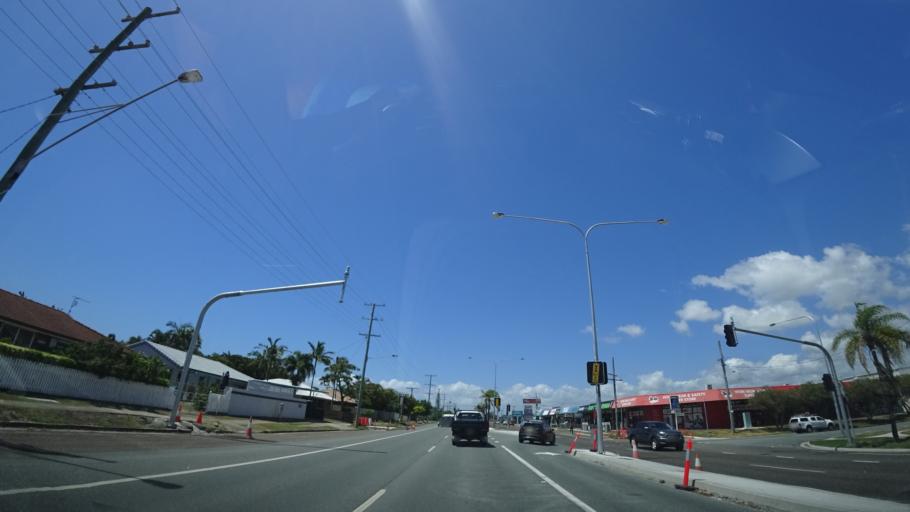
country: AU
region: Queensland
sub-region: Sunshine Coast
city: Mooloolaba
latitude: -26.7274
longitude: 153.1293
